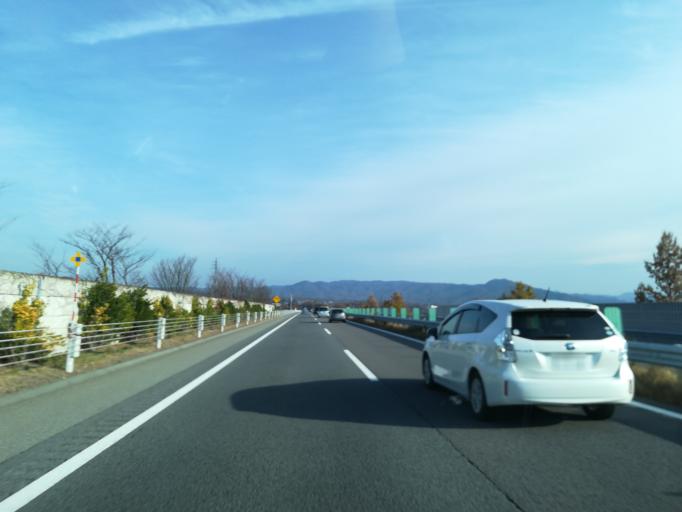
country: JP
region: Nagano
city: Komoro
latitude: 36.3281
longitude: 138.4587
